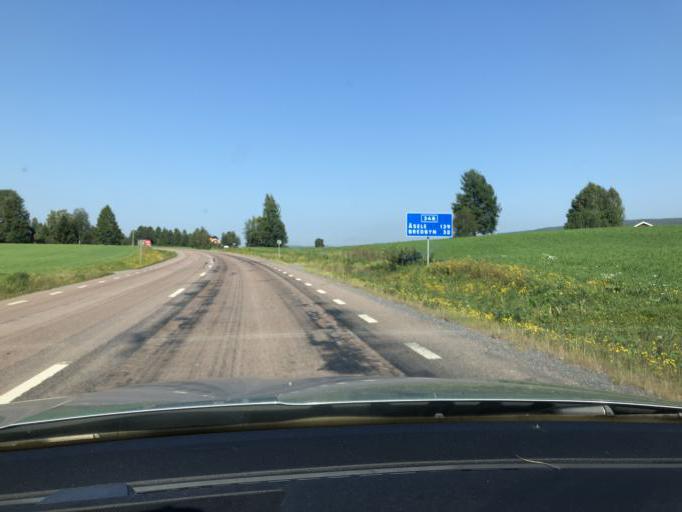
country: SE
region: Vaesternorrland
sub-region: OErnskoeldsviks Kommun
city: Bjasta
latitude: 63.2881
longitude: 18.5659
